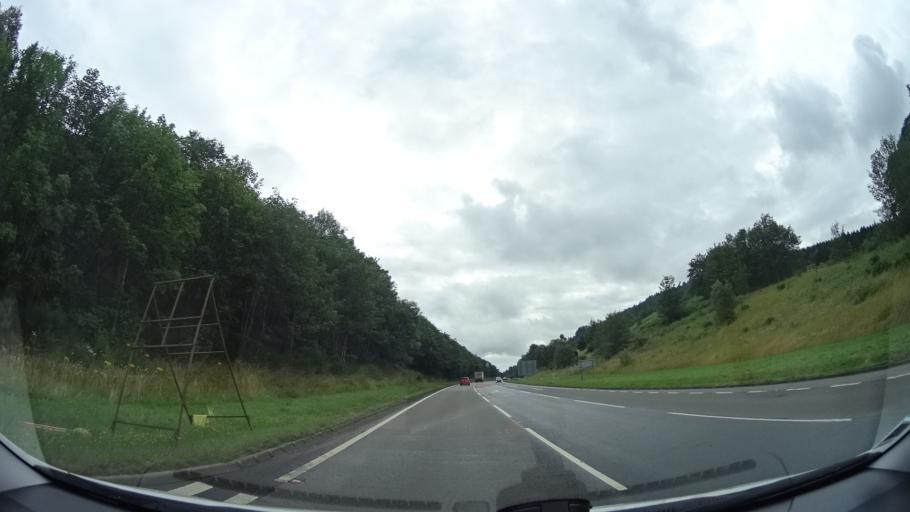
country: GB
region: Scotland
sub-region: Perth and Kinross
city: Bankfoot
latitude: 56.5605
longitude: -3.5866
